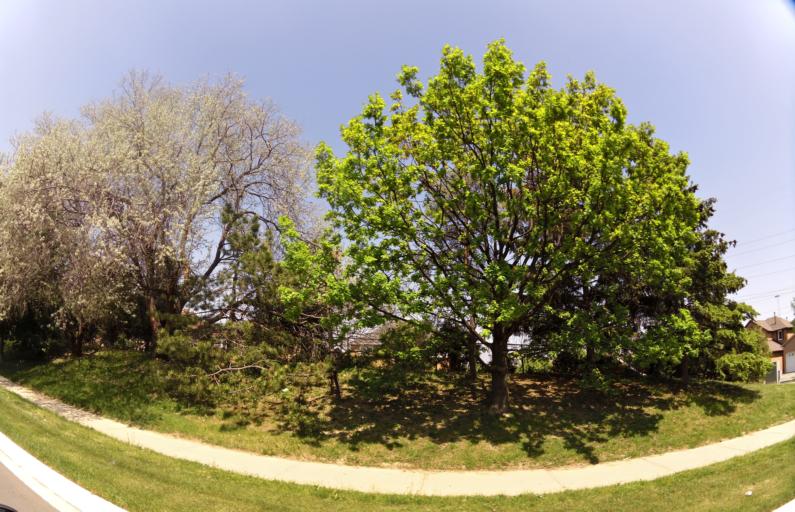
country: CA
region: Ontario
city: Mississauga
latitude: 43.6098
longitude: -79.6390
